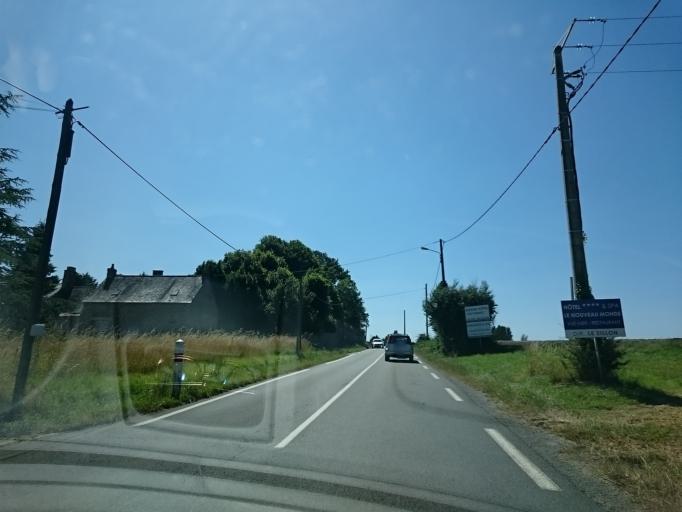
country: FR
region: Brittany
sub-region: Departement d'Ille-et-Vilaine
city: Saint-Coulomb
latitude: 48.6670
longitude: -1.9540
